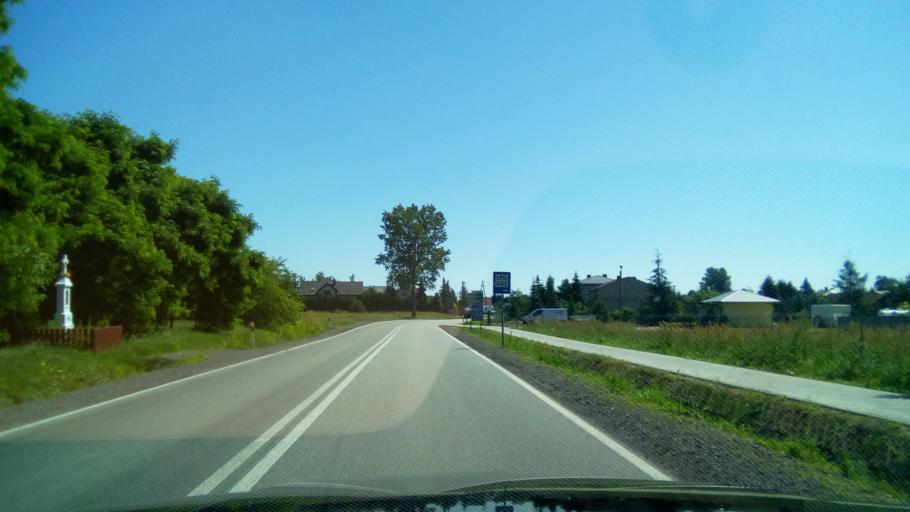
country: PL
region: Masovian Voivodeship
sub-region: Powiat przysuski
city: Odrzywol
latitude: 51.5179
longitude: 20.5450
